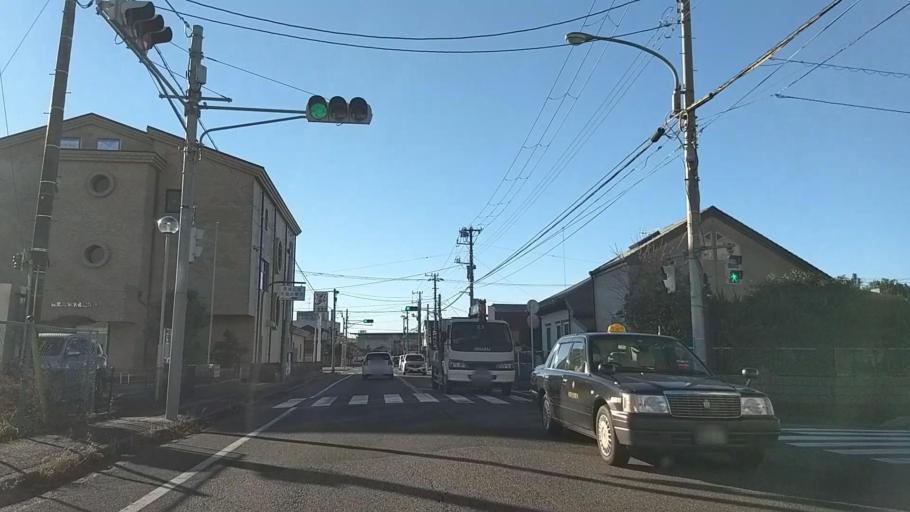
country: JP
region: Chiba
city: Kisarazu
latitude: 35.3783
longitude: 139.9186
